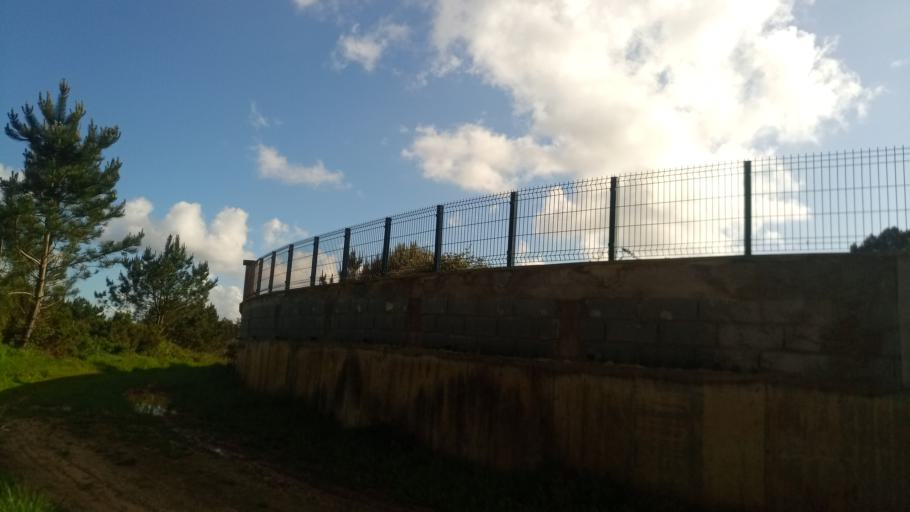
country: PT
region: Leiria
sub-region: Caldas da Rainha
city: Caldas da Rainha
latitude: 39.4567
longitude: -9.1984
